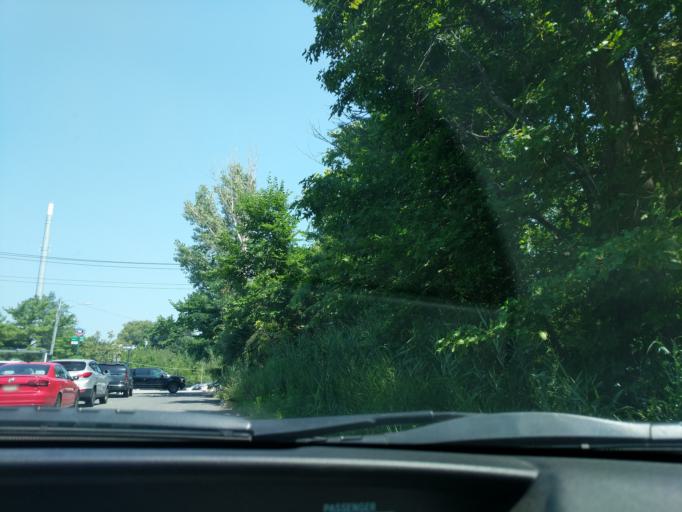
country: US
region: New Jersey
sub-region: Middlesex County
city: Carteret
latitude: 40.5341
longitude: -74.1922
